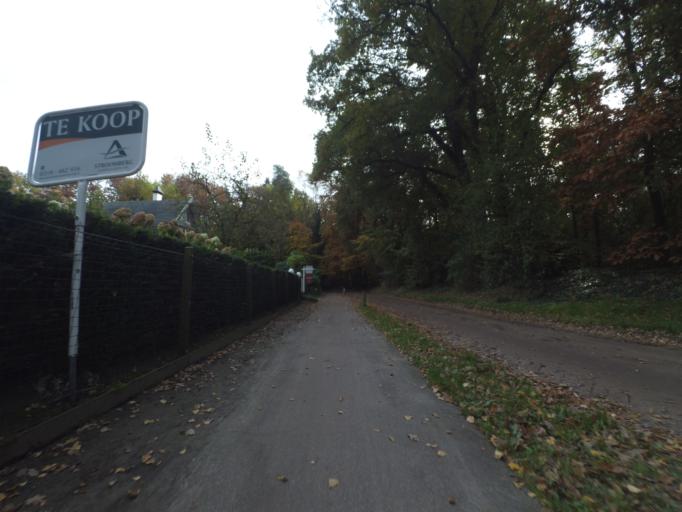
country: NL
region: Gelderland
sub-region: Gemeente Ede
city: Lunteren
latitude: 52.0898
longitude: 5.6324
